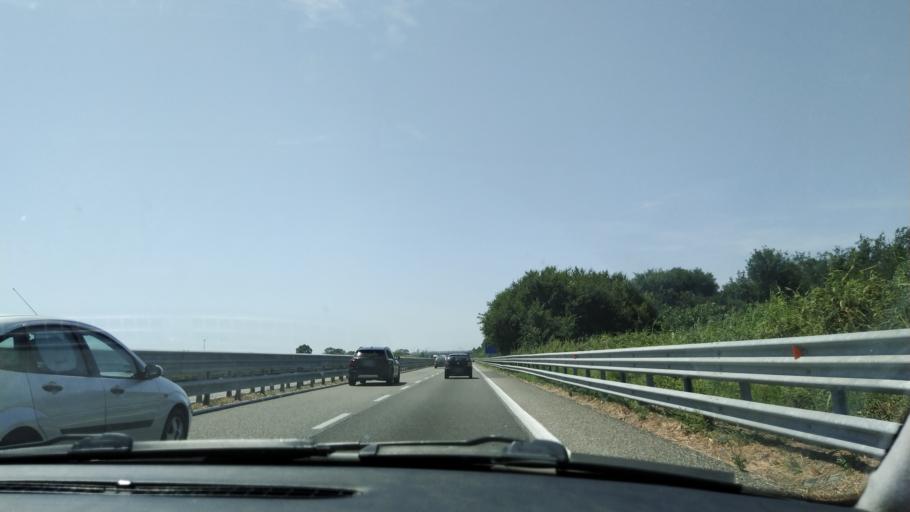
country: IT
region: Basilicate
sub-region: Provincia di Matera
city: Marconia
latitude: 40.3461
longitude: 16.7660
